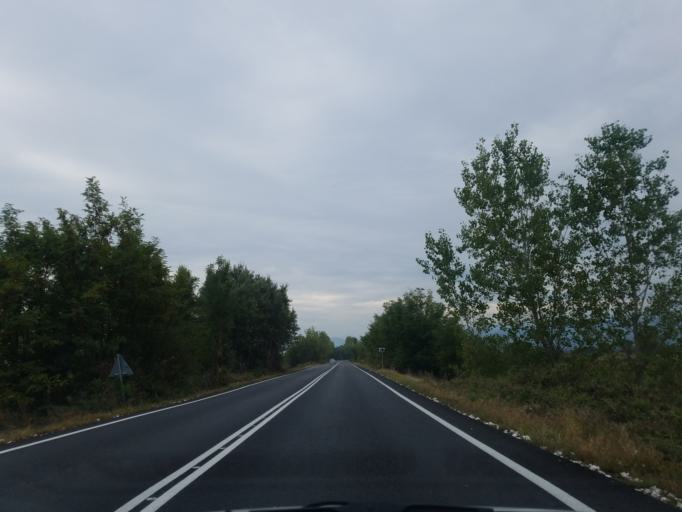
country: GR
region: Thessaly
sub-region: Nomos Kardhitsas
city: Agnantero
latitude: 39.5021
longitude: 21.8397
